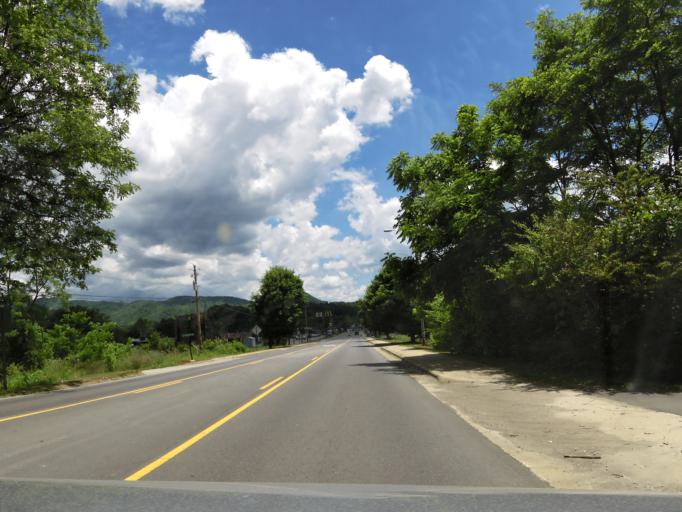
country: US
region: North Carolina
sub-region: Graham County
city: Robbinsville
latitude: 35.3281
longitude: -83.8064
